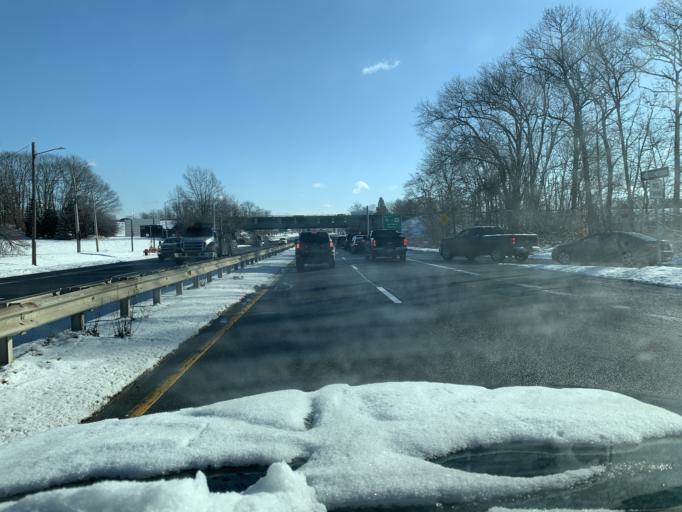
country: US
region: Massachusetts
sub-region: Essex County
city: Danvers
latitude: 42.5602
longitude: -70.9763
